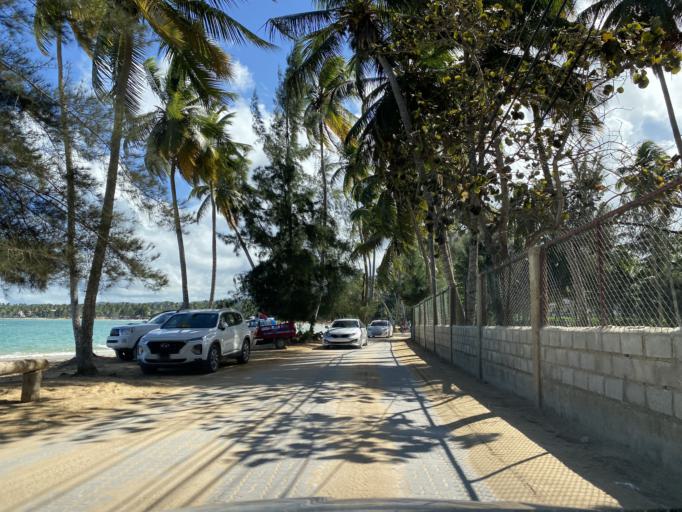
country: DO
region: Samana
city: Las Terrenas
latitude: 19.3250
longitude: -69.5438
